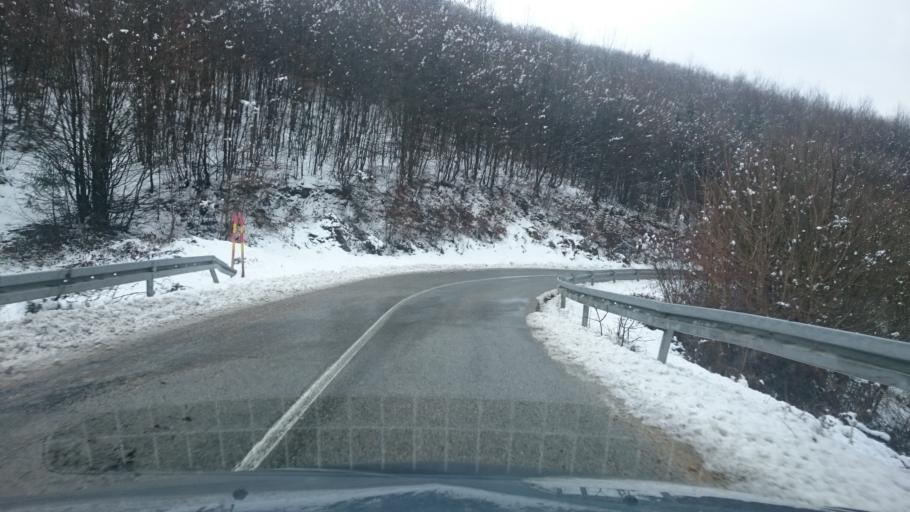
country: BA
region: Republika Srpska
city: Starcevica
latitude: 44.6793
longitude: 17.2134
